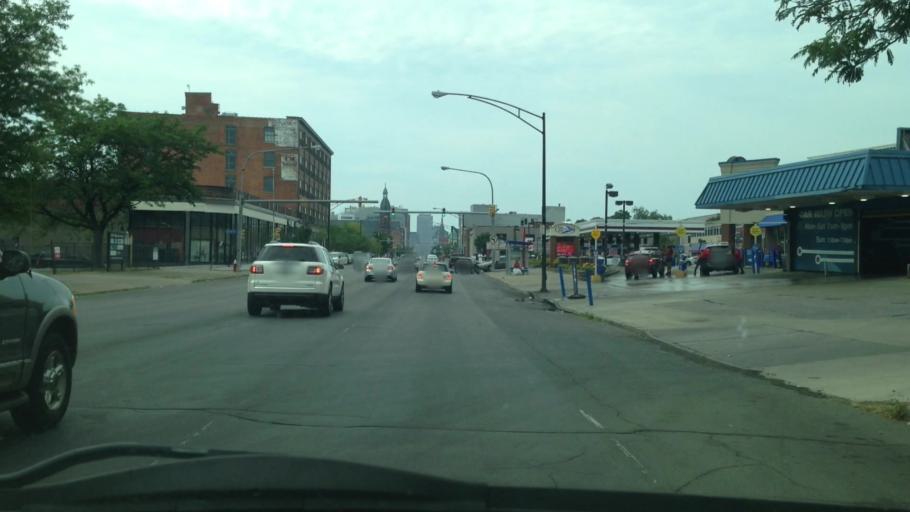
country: US
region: New York
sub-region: Erie County
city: Buffalo
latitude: 42.9084
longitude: -78.8669
